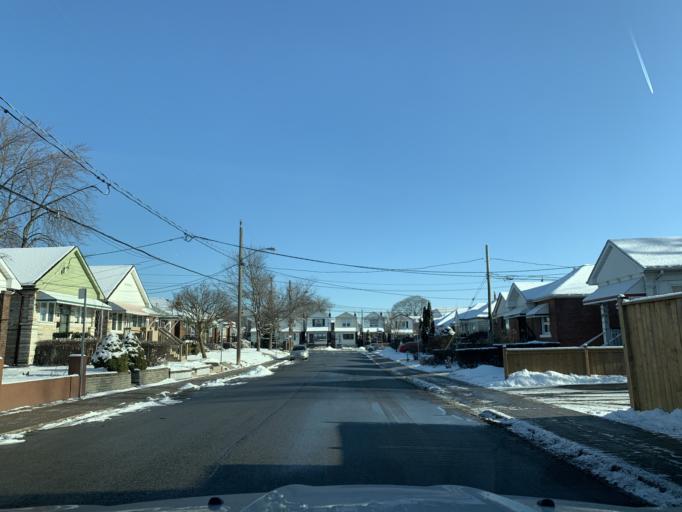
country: CA
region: Ontario
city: Toronto
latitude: 43.6707
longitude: -79.4878
